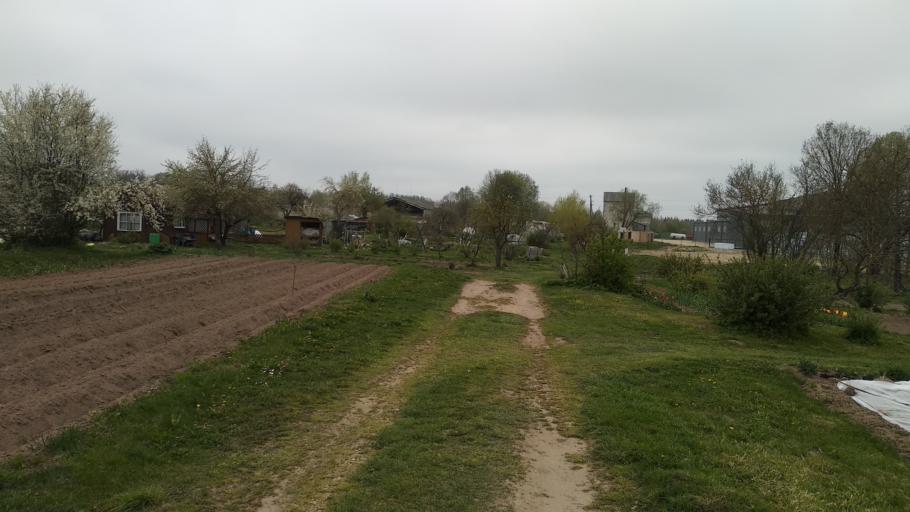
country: LV
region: Malpils
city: Malpils
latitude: 57.0140
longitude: 24.9591
